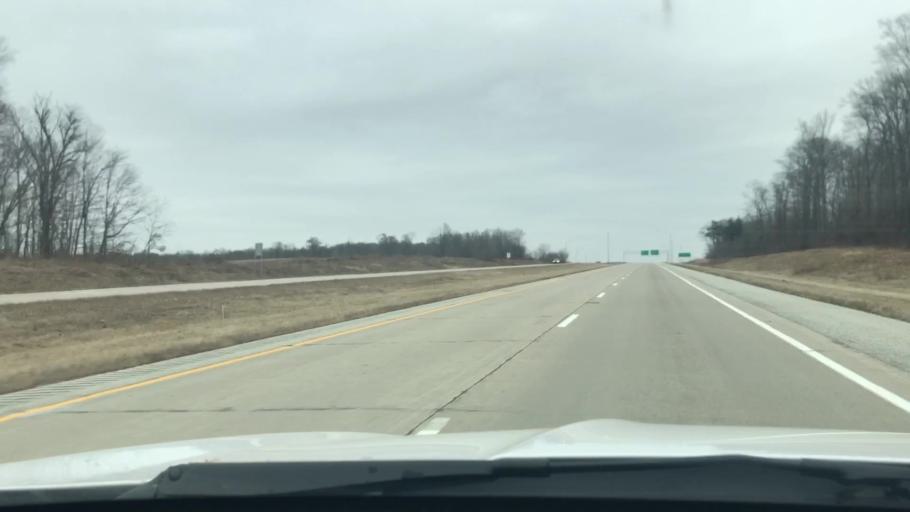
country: US
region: Indiana
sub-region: Miami County
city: Peru
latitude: 40.7709
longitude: -86.1424
